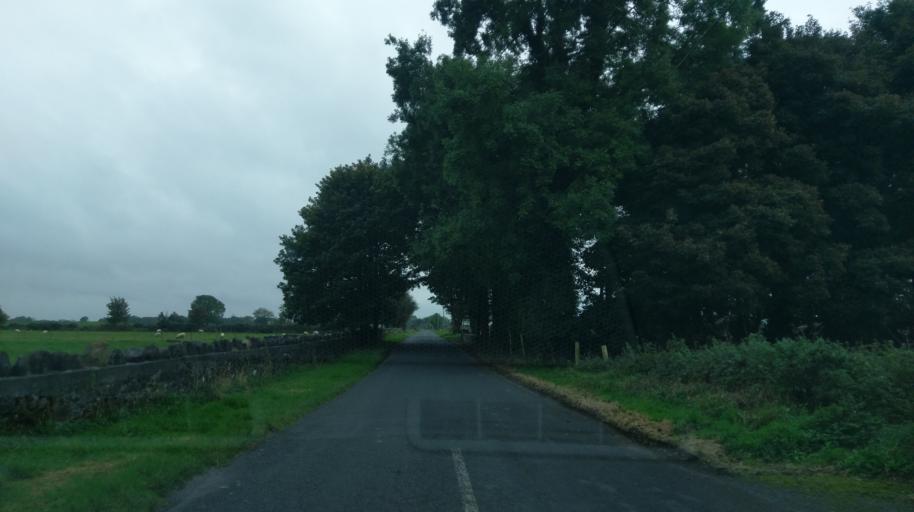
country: IE
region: Connaught
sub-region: County Galway
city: Athenry
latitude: 53.4565
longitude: -8.6024
